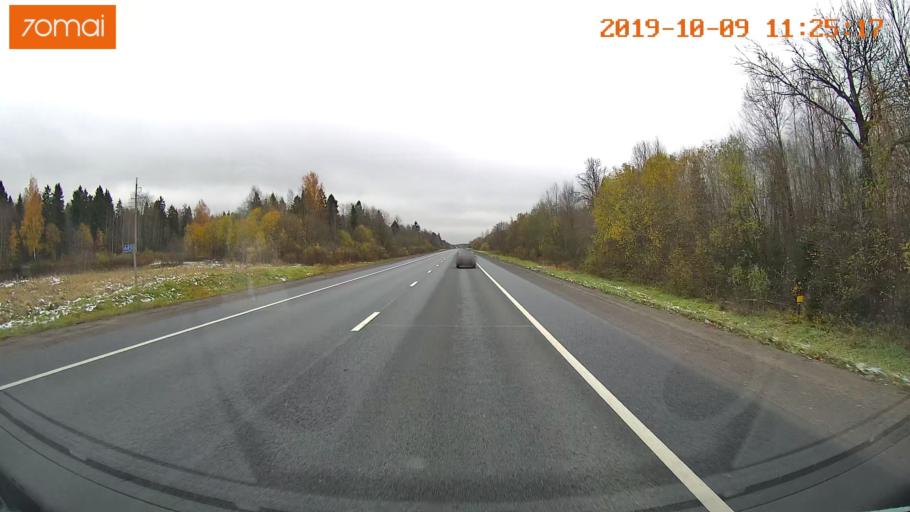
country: RU
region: Vologda
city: Vologda
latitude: 59.1024
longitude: 39.9899
